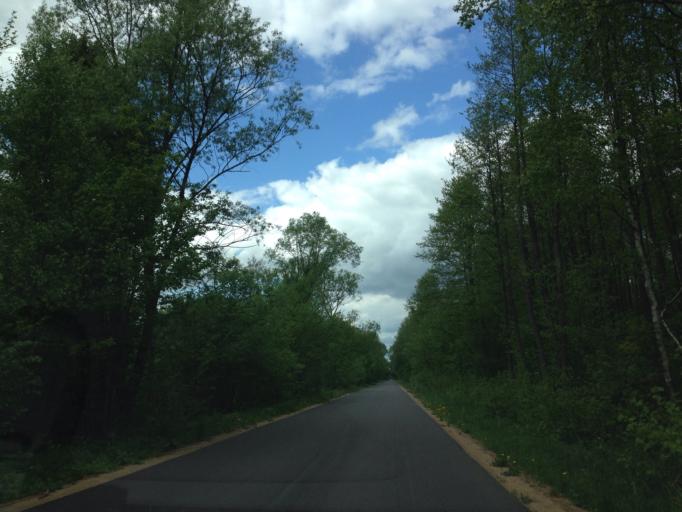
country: PL
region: Podlasie
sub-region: Powiat grajewski
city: Radzilow
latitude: 53.3237
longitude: 22.6011
